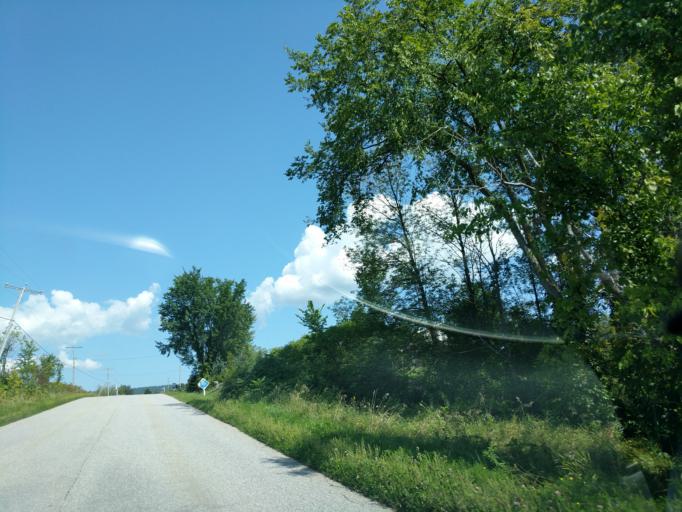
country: CA
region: Quebec
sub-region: Outaouais
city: Wakefield
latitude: 45.4955
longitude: -75.9525
